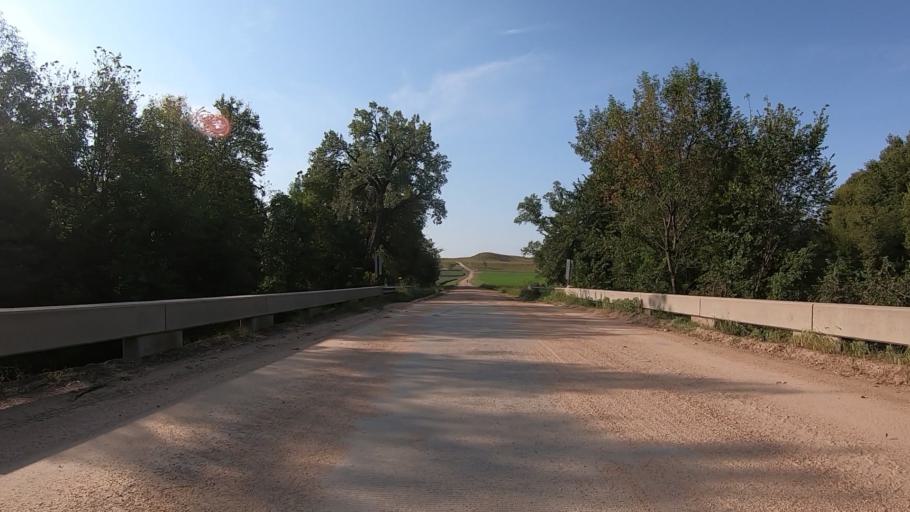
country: US
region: Kansas
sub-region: Marshall County
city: Blue Rapids
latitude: 39.6553
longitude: -96.8815
